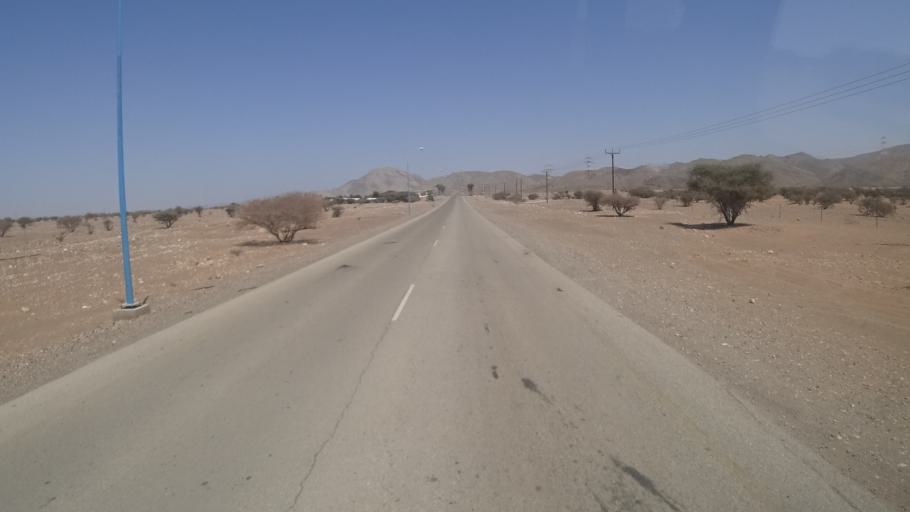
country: OM
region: Ash Sharqiyah
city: Badiyah
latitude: 22.5076
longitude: 58.9475
